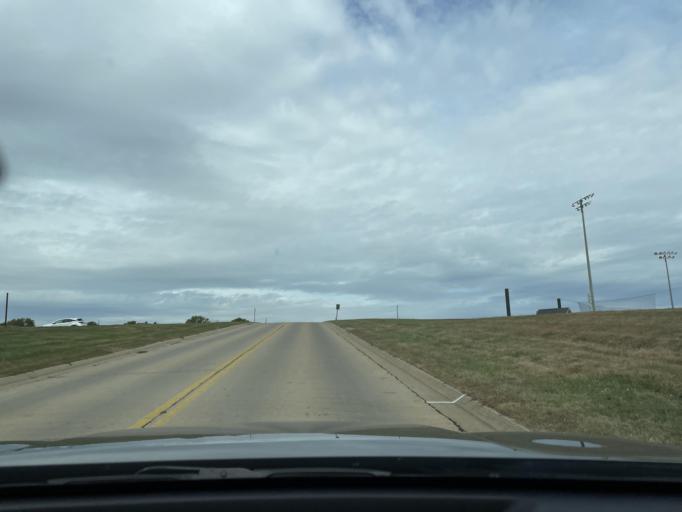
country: US
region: Missouri
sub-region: Buchanan County
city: Saint Joseph
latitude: 39.7665
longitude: -94.7810
